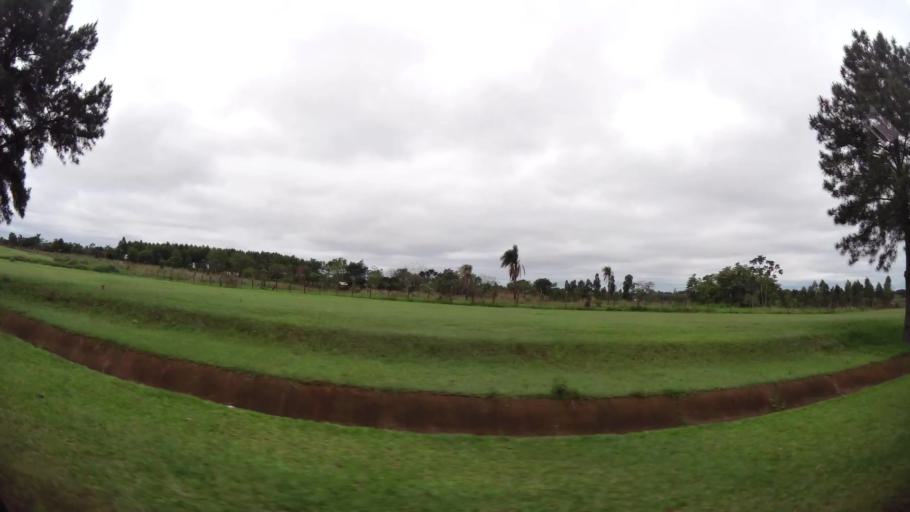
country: PY
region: Alto Parana
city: Colonia Yguazu
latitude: -25.4768
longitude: -54.8606
